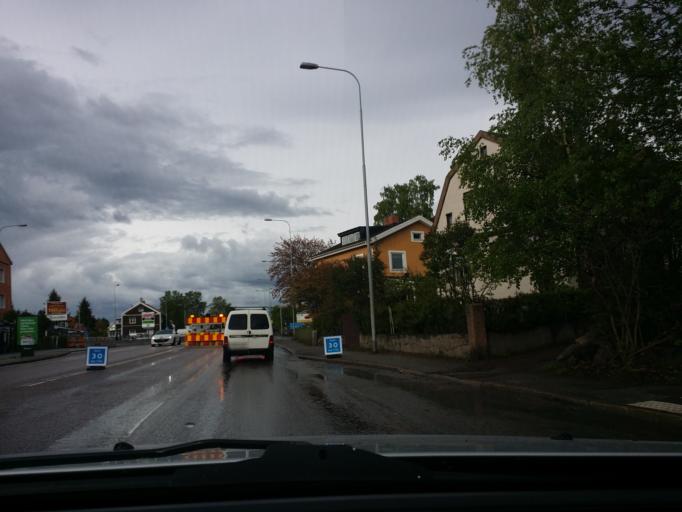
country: SE
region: Vaestmanland
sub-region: Vasteras
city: Vasteras
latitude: 59.6205
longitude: 16.5721
